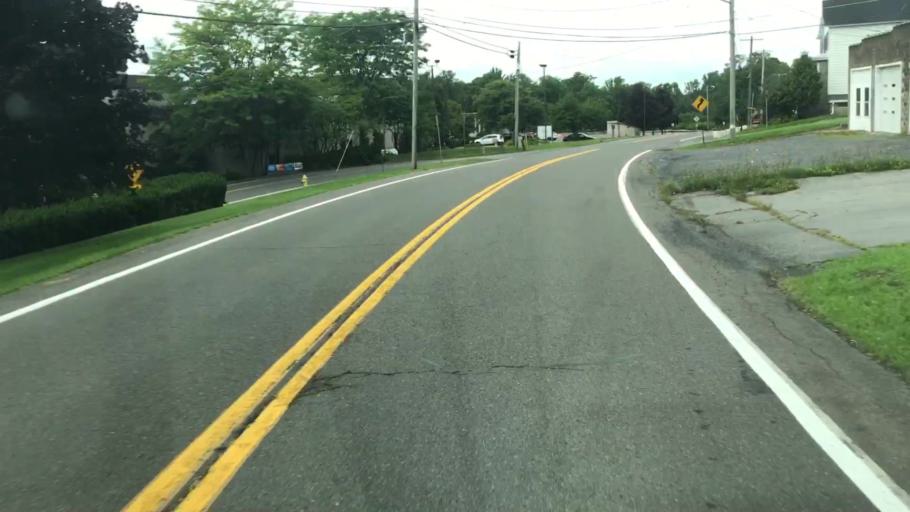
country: US
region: New York
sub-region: Onondaga County
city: Elbridge
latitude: 42.9939
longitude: -76.4573
